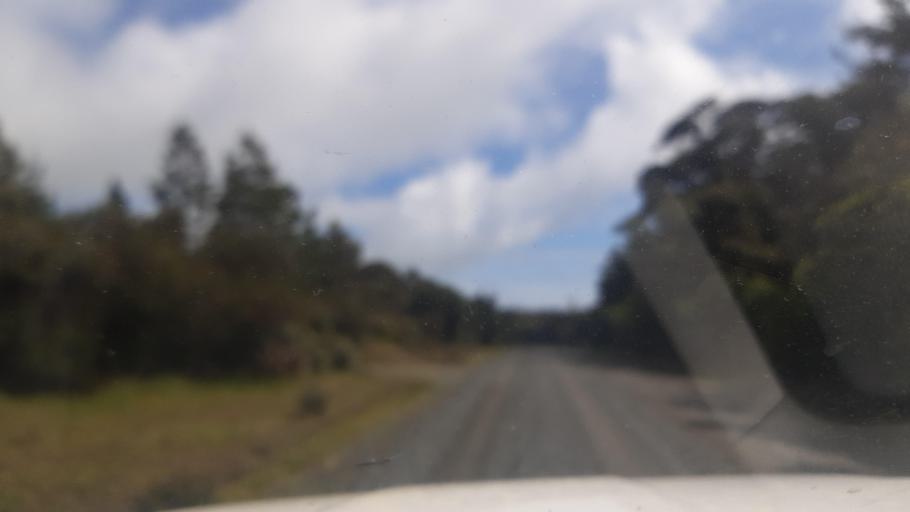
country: NZ
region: Northland
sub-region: Far North District
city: Kaitaia
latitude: -34.7401
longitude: 173.1114
